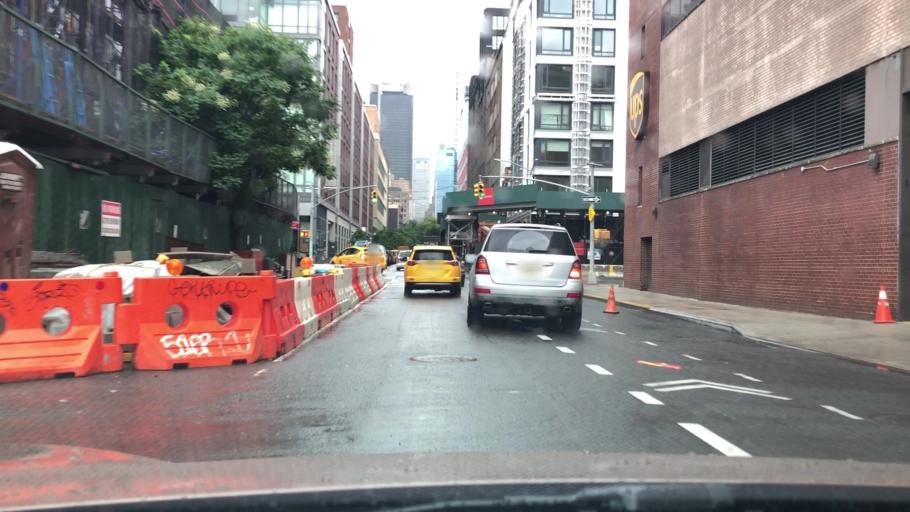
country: US
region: New Jersey
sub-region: Hudson County
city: Weehawken
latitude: 40.7624
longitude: -73.9979
